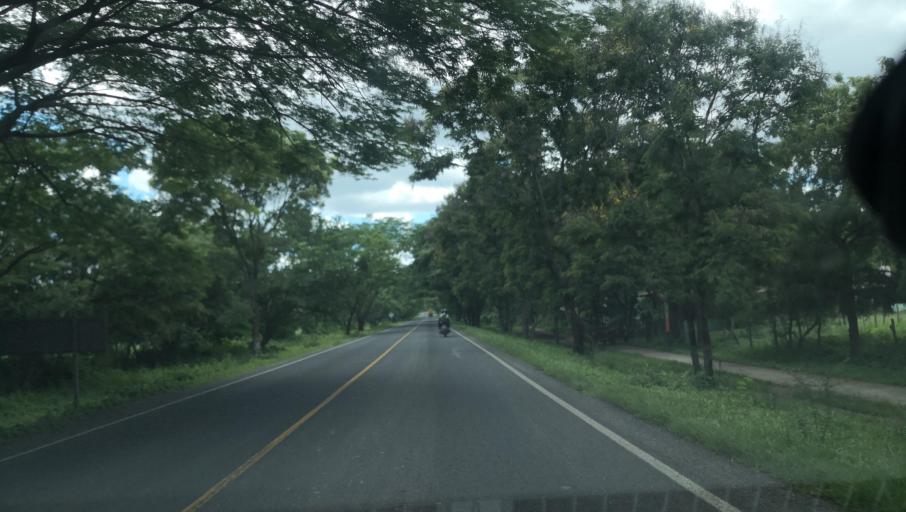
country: NI
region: Madriz
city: Palacaguina
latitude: 13.4517
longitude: -86.4449
